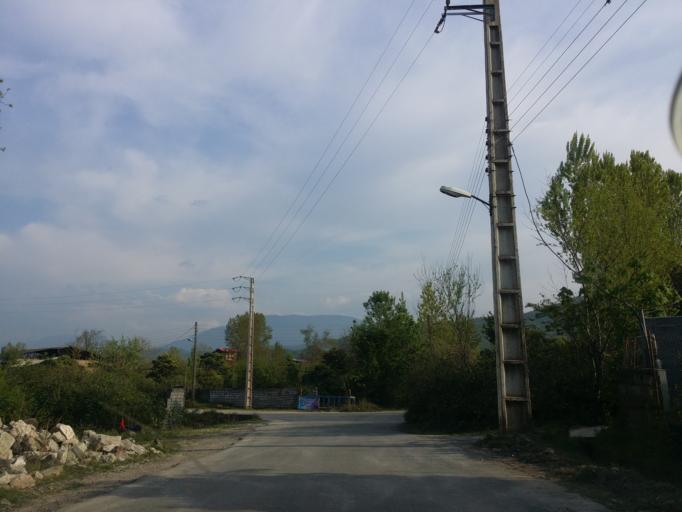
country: IR
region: Mazandaran
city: Chalus
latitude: 36.6580
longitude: 51.3904
